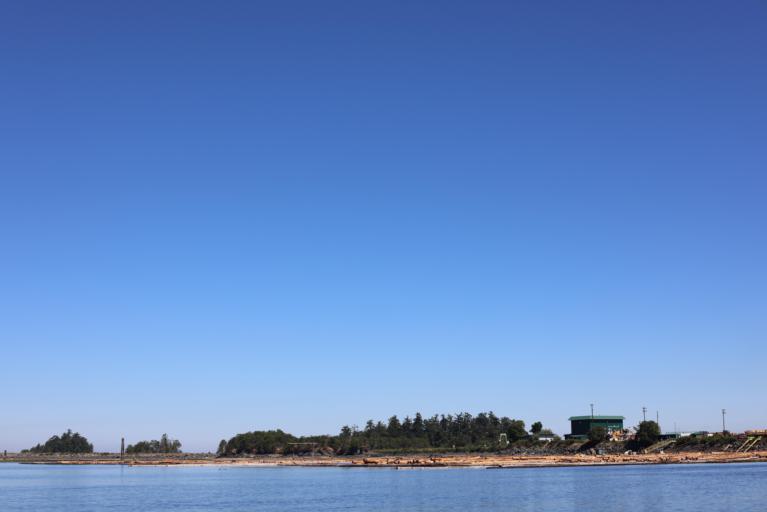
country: CA
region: British Columbia
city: North Cowichan
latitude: 48.8781
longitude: -123.6369
